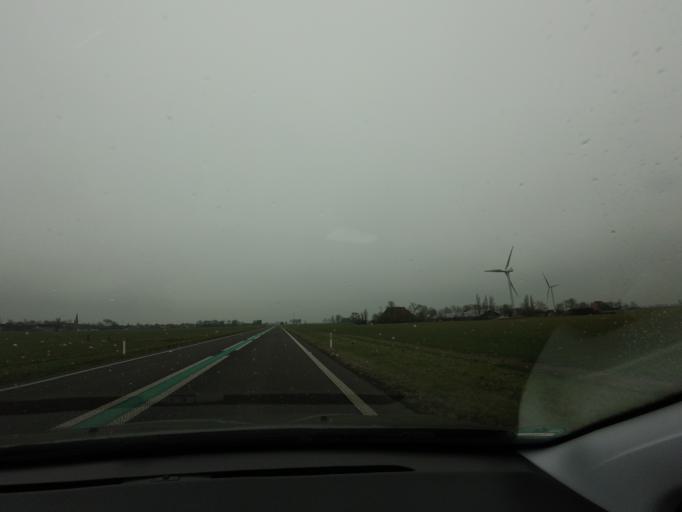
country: NL
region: Friesland
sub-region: Gemeente Littenseradiel
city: Wommels
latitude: 53.1158
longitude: 5.5864
